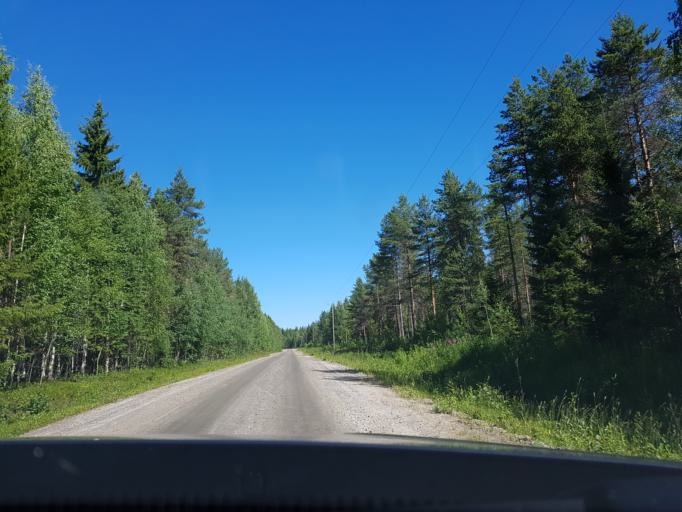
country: FI
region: Kainuu
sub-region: Kehys-Kainuu
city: Kuhmo
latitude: 64.1901
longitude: 29.6009
